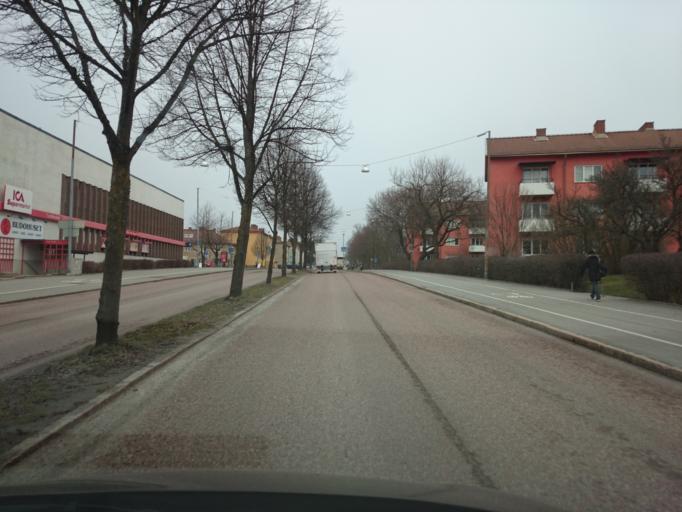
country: SE
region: Uppsala
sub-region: Uppsala Kommun
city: Uppsala
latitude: 59.8741
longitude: 17.6253
